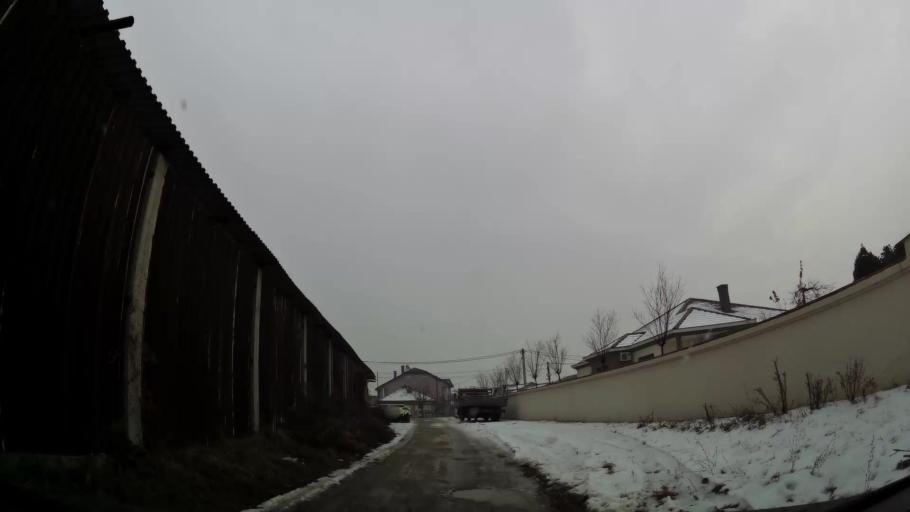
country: MK
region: Petrovec
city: Petrovec
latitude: 41.9343
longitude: 21.6153
